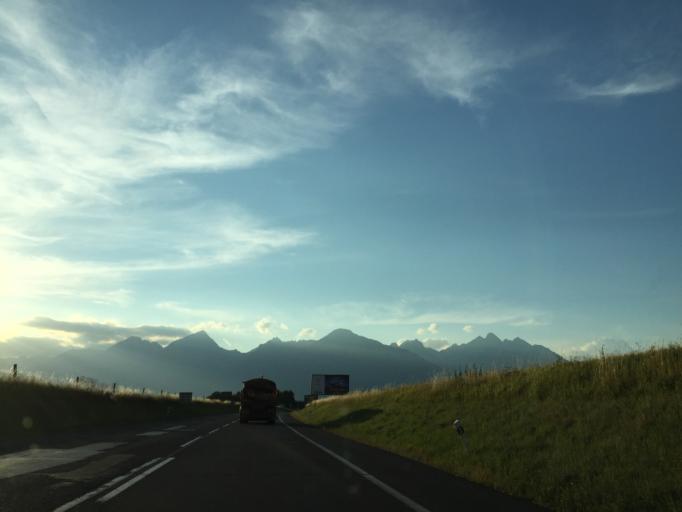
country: SK
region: Presovsky
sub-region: Okres Poprad
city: Poprad
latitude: 49.0756
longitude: 20.2735
